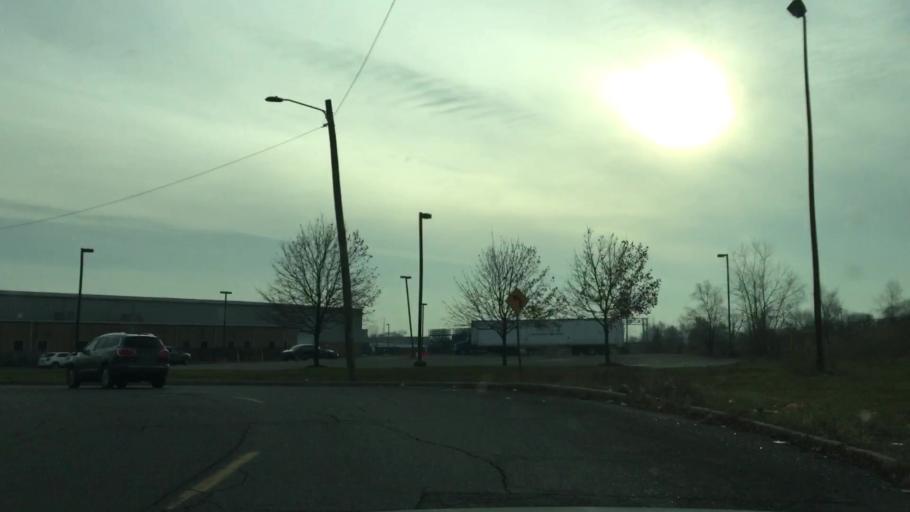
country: US
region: Michigan
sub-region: Wayne County
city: Detroit
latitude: 42.3304
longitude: -83.1028
